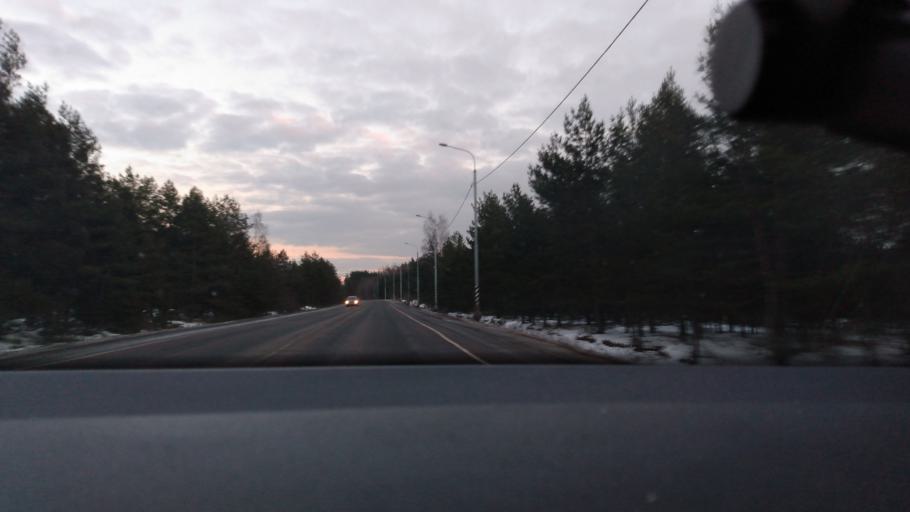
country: RU
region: Moskovskaya
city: Il'inskiy Pogost
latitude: 55.5003
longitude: 38.8079
